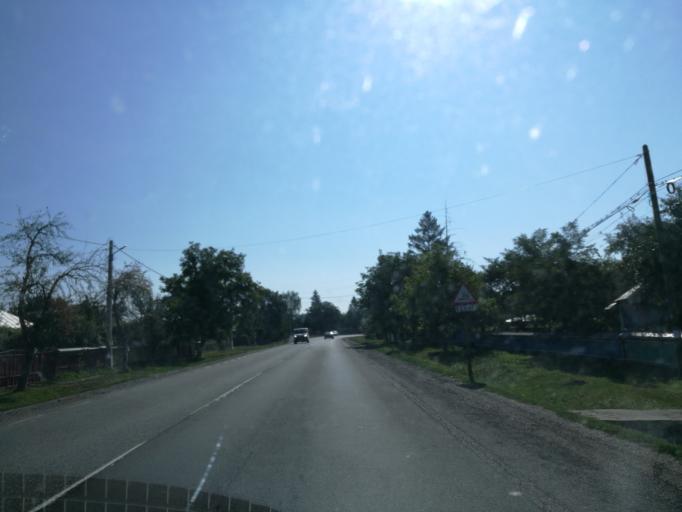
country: RO
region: Suceava
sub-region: Comuna Vadu Moldovei
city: Vadu Moldovei
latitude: 47.3816
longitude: 26.3621
